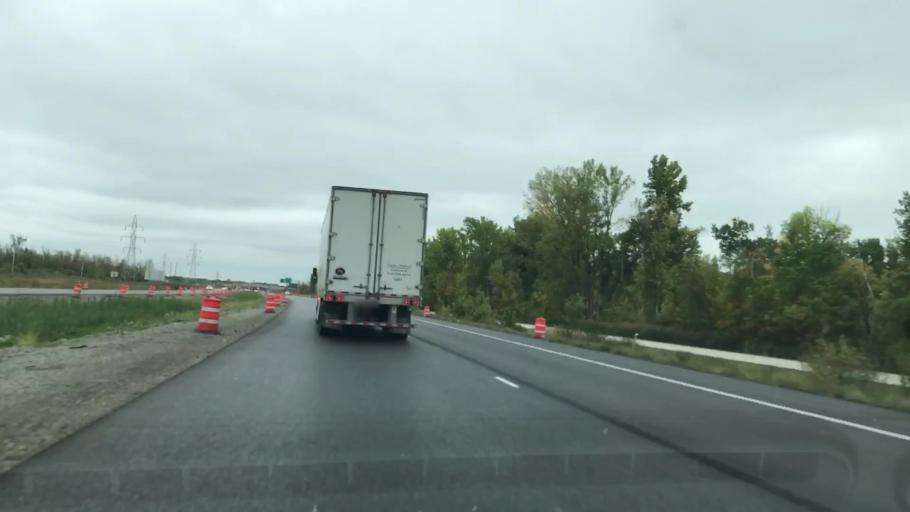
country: US
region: Wisconsin
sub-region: Brown County
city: Suamico
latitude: 44.6023
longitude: -88.0504
